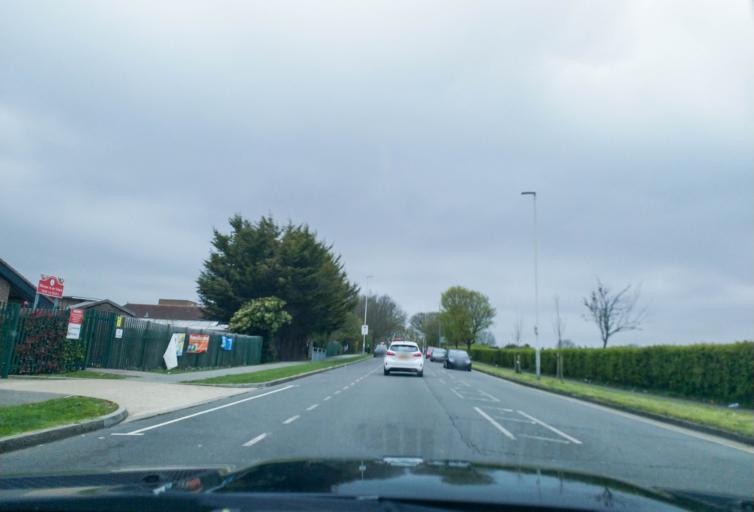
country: GB
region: England
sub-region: Greater London
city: Northolt
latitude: 51.5664
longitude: -0.3864
